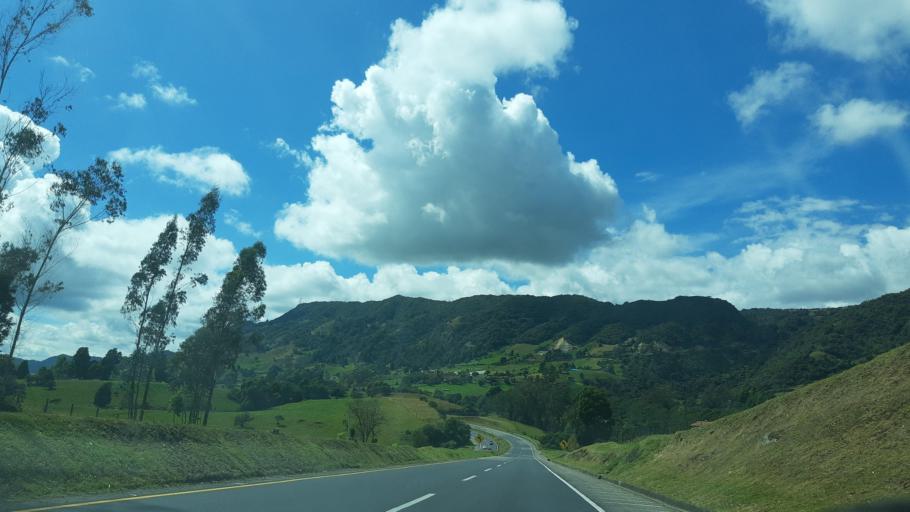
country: CO
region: Boyaca
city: Ventaquemada
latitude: 5.3981
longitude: -73.4896
